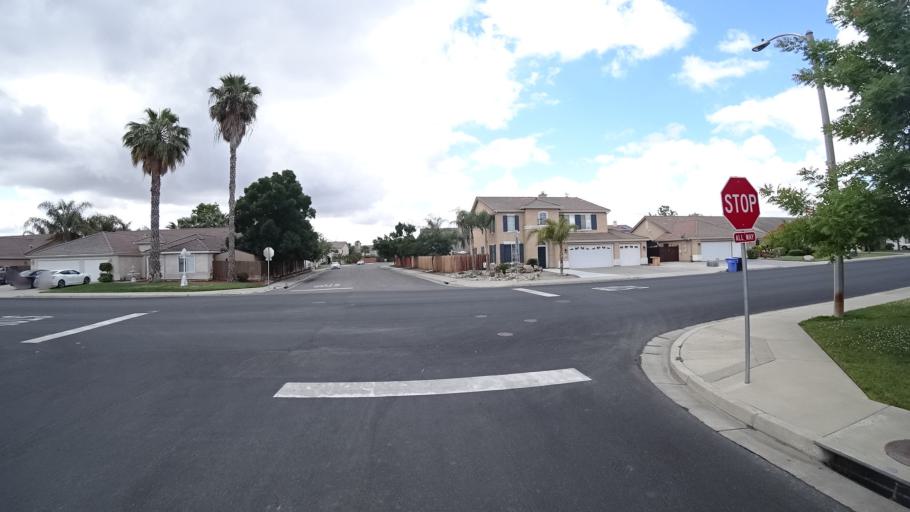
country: US
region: California
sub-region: Kings County
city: Lucerne
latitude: 36.3635
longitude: -119.6568
